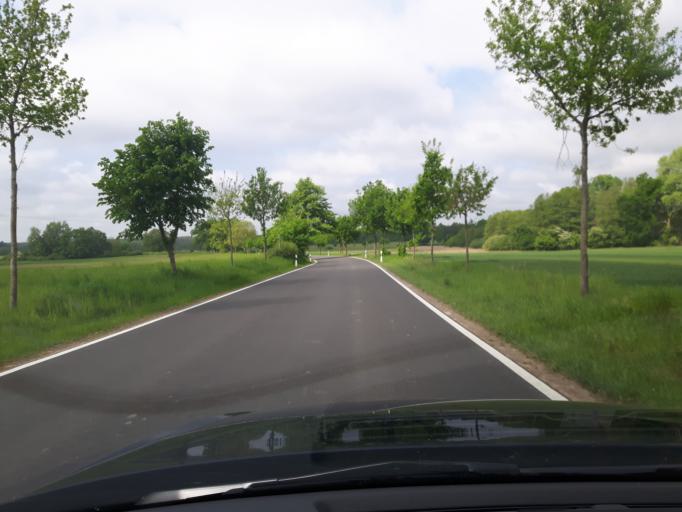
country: DE
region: Mecklenburg-Vorpommern
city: Grabowhofe
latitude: 53.5799
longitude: 12.5159
